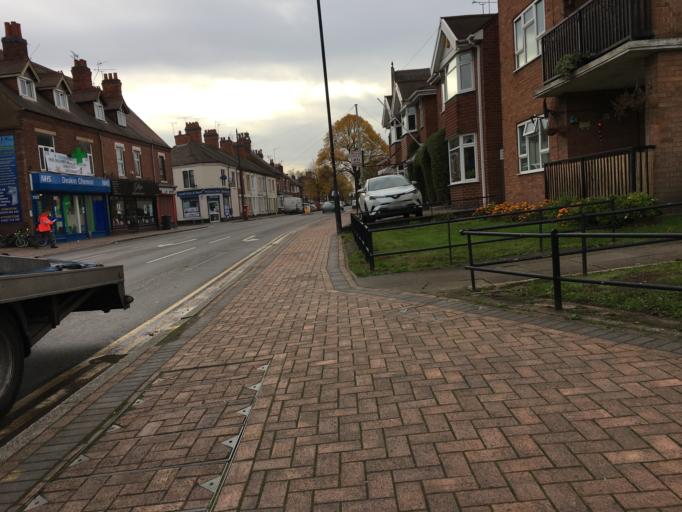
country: GB
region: England
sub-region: Warwickshire
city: Nuneaton
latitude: 52.5276
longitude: -1.4758
